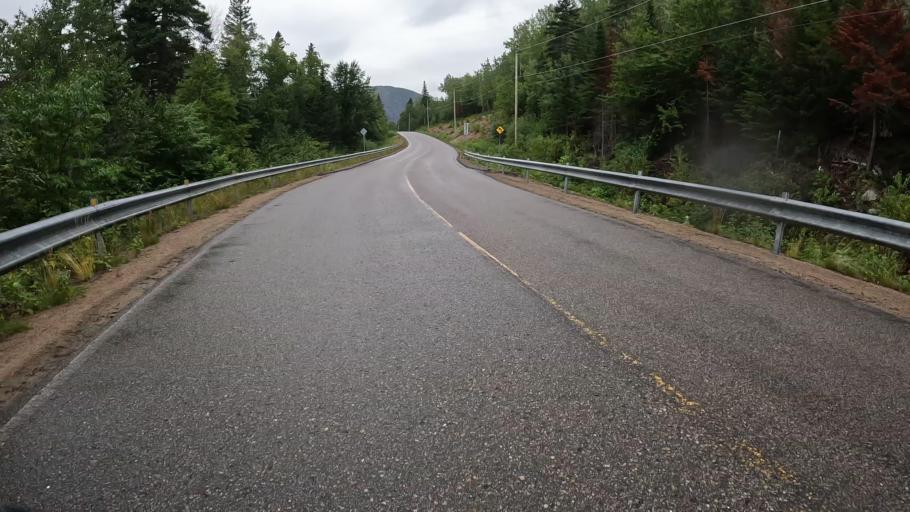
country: CA
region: Quebec
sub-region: Capitale-Nationale
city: La Malbaie
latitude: 47.8591
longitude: -70.4689
